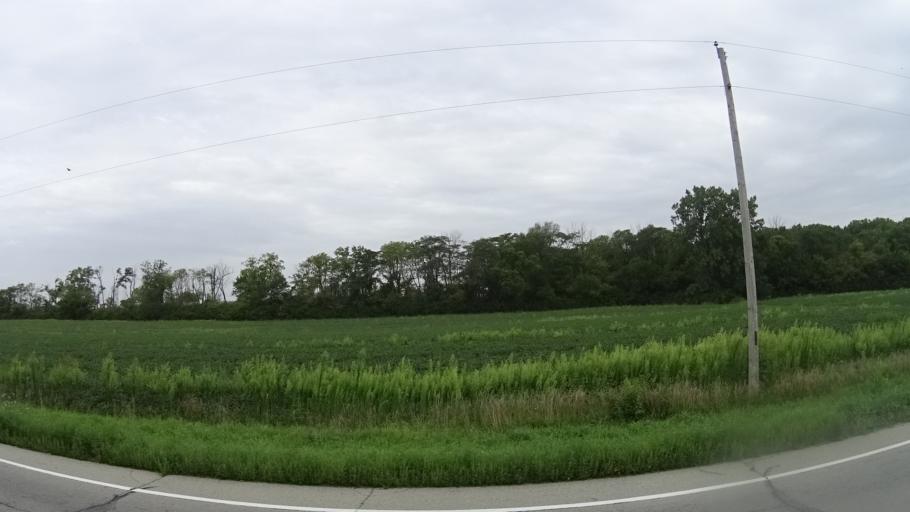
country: US
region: Indiana
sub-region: Madison County
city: Lapel
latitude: 40.0945
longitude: -85.8123
